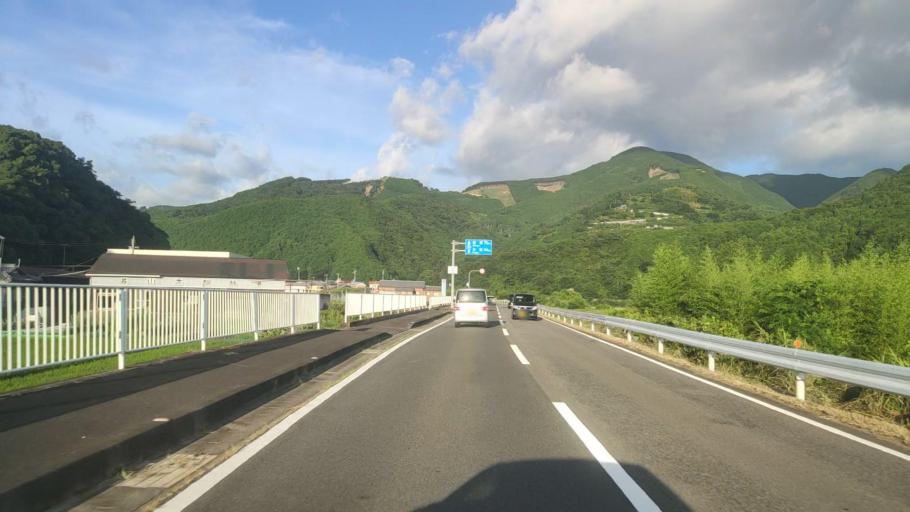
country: JP
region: Wakayama
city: Tanabe
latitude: 33.7186
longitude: 135.4766
